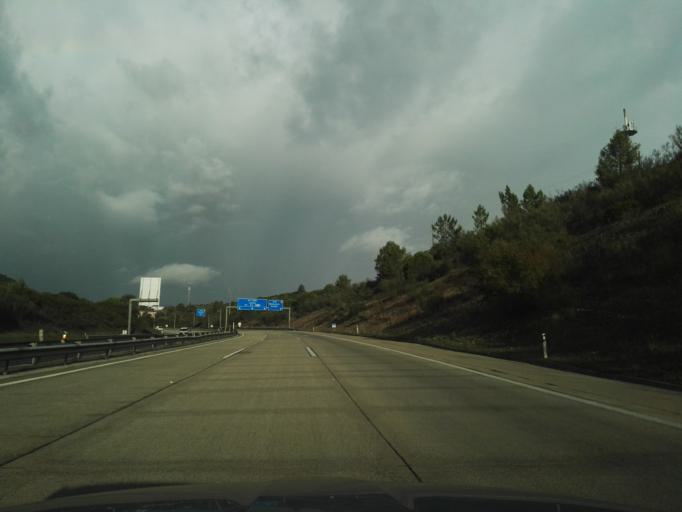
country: PT
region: Lisbon
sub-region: Vila Franca de Xira
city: Vialonga
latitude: 38.9083
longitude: -9.0657
